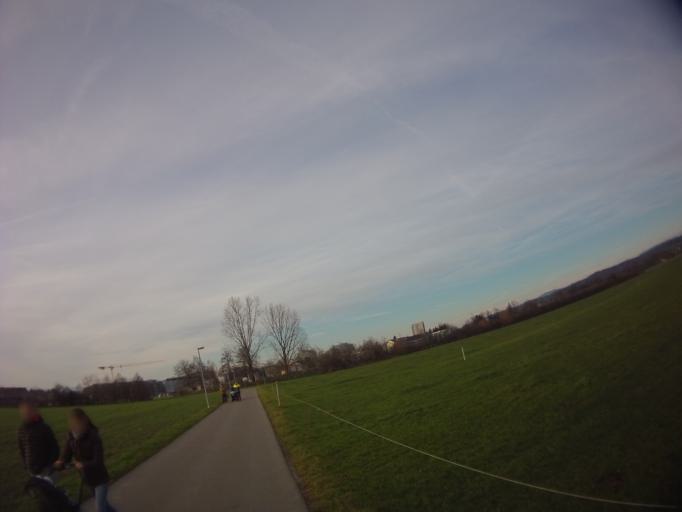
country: CH
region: Zug
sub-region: Zug
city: Steinhausen
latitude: 47.1800
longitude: 8.4970
